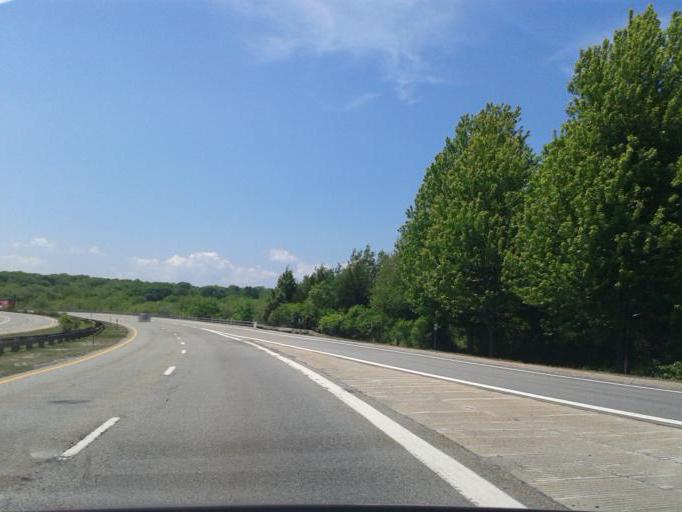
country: US
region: Rhode Island
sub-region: Newport County
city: Jamestown
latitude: 41.5258
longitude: -71.3699
